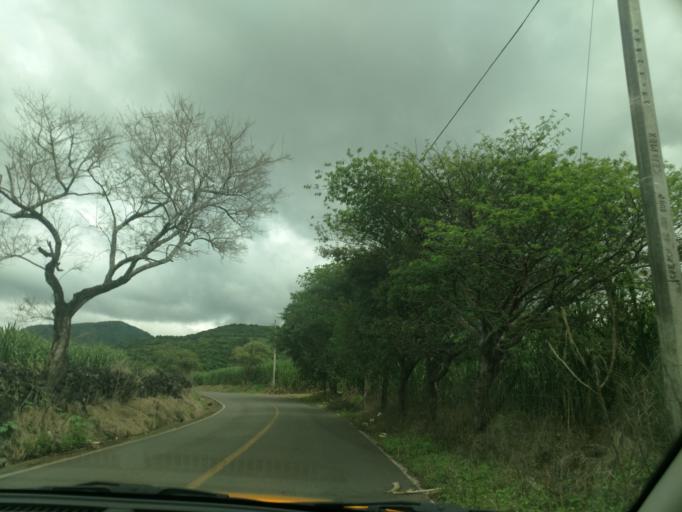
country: MX
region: Nayarit
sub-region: Tepic
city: La Corregidora
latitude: 21.4562
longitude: -104.8014
